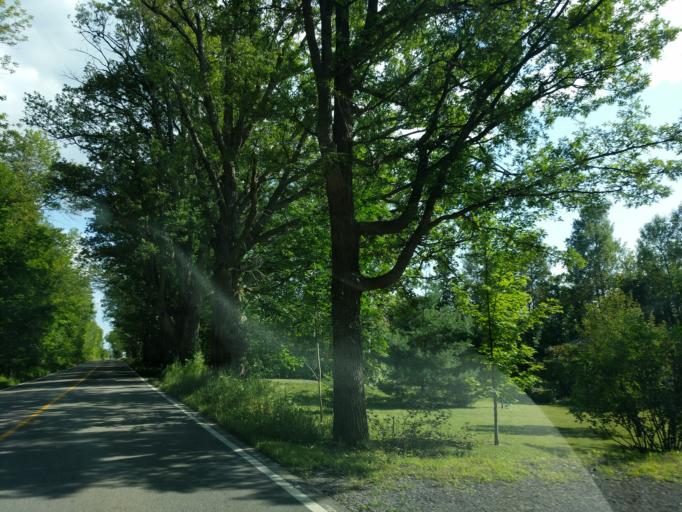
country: CA
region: Quebec
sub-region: Outaouais
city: Gatineau
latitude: 45.4769
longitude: -75.8585
